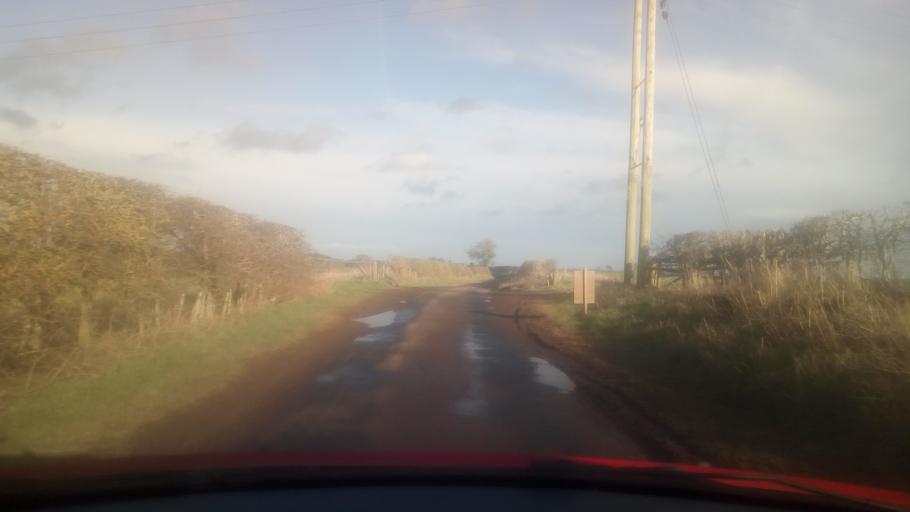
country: GB
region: Scotland
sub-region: The Scottish Borders
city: Duns
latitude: 55.7364
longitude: -2.3532
